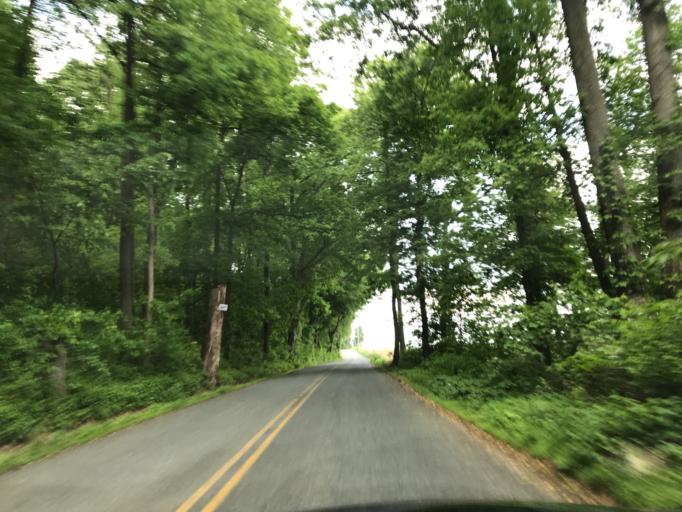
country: US
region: Pennsylvania
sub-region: York County
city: Susquehanna Trails
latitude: 39.7107
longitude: -76.3240
